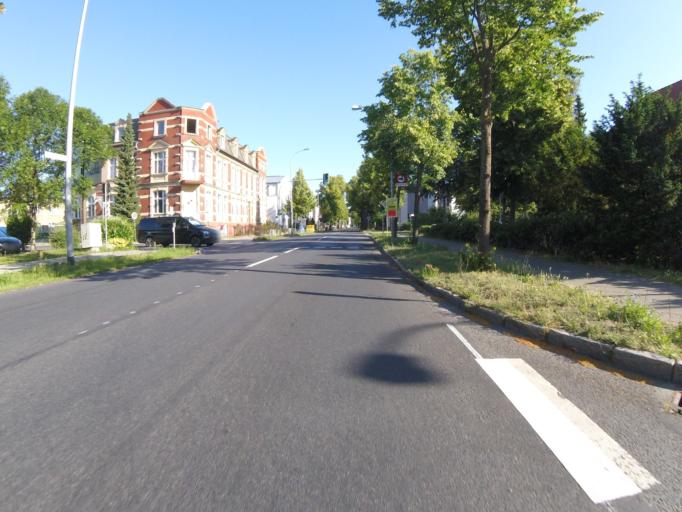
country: DE
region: Brandenburg
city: Konigs Wusterhausen
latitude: 52.2924
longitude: 13.6268
